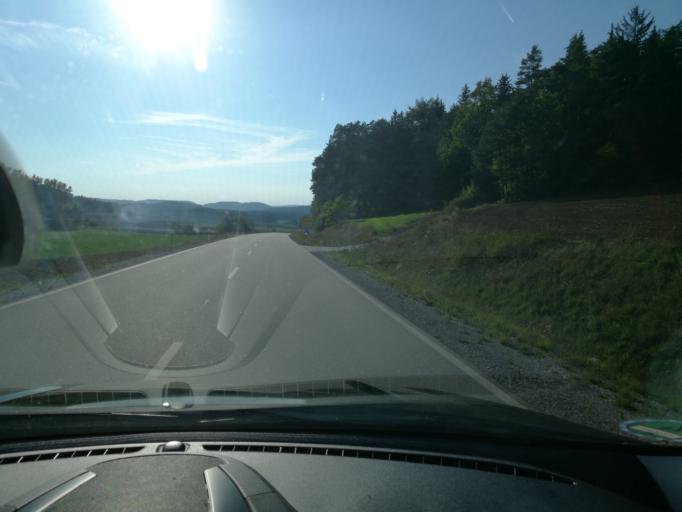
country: DE
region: Bavaria
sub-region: Upper Palatinate
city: Hohenfels
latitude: 49.1860
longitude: 11.8013
